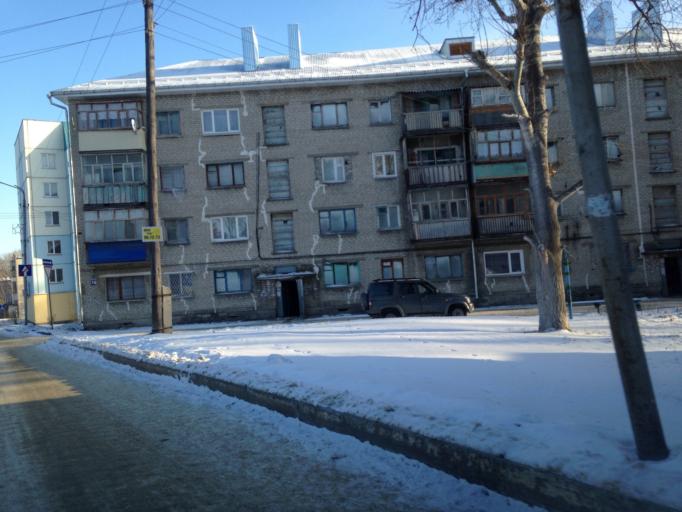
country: RU
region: Ulyanovsk
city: Novoul'yanovsk
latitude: 54.1535
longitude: 48.3812
